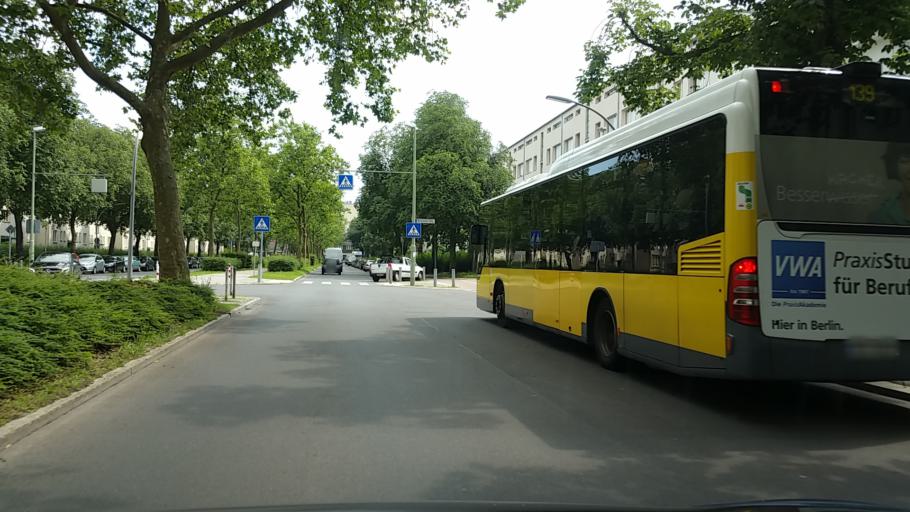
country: DE
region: Berlin
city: Haselhorst
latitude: 52.5451
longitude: 13.2380
